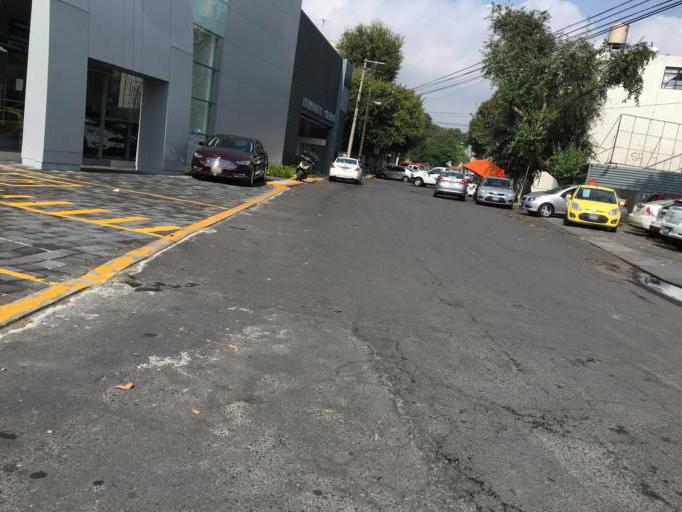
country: MX
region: Mexico City
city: Tlalpan
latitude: 19.2836
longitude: -99.1453
